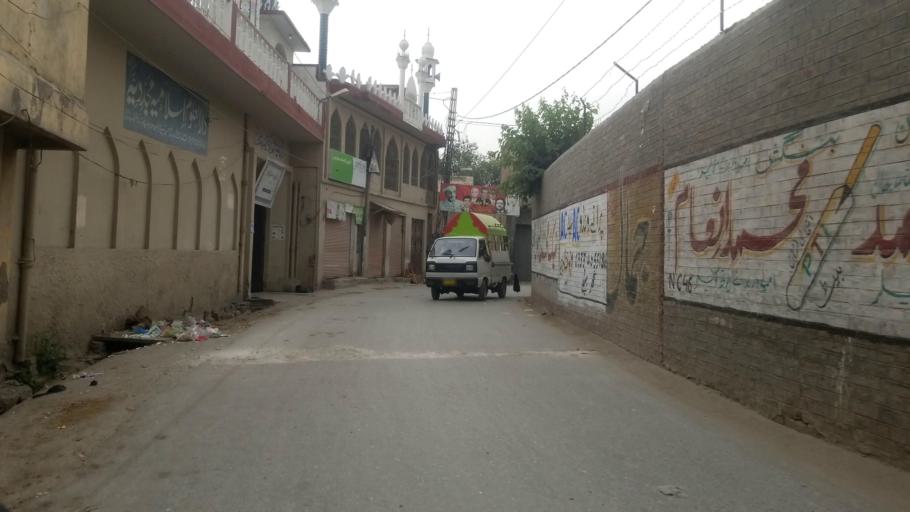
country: PK
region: Khyber Pakhtunkhwa
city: Peshawar
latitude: 33.9932
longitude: 71.5635
